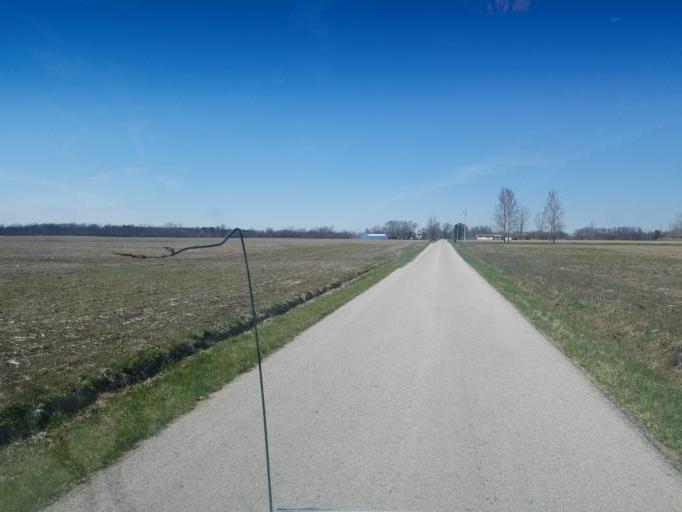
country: US
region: Ohio
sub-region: Morrow County
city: Cardington
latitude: 40.5388
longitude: -82.9104
